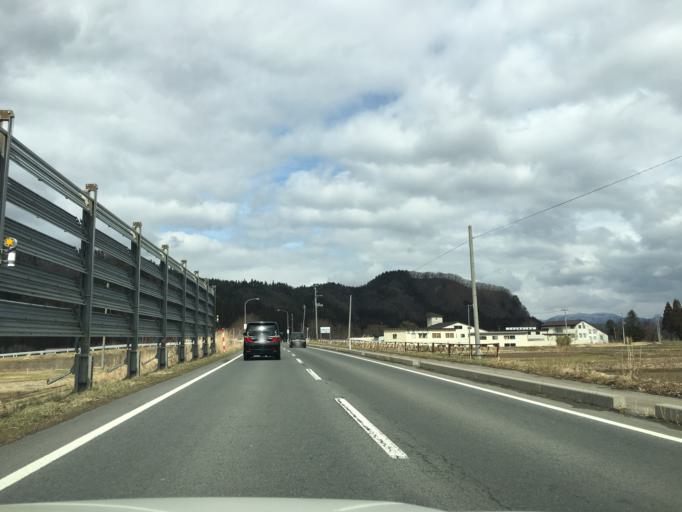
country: JP
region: Akita
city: Hanawa
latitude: 40.2414
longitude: 140.7390
